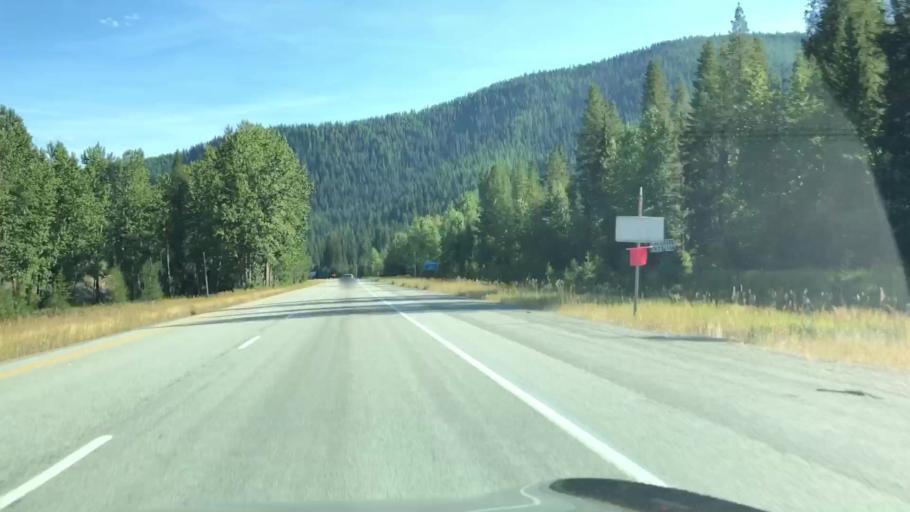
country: US
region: Idaho
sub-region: Shoshone County
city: Wallace
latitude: 47.4281
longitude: -115.6401
